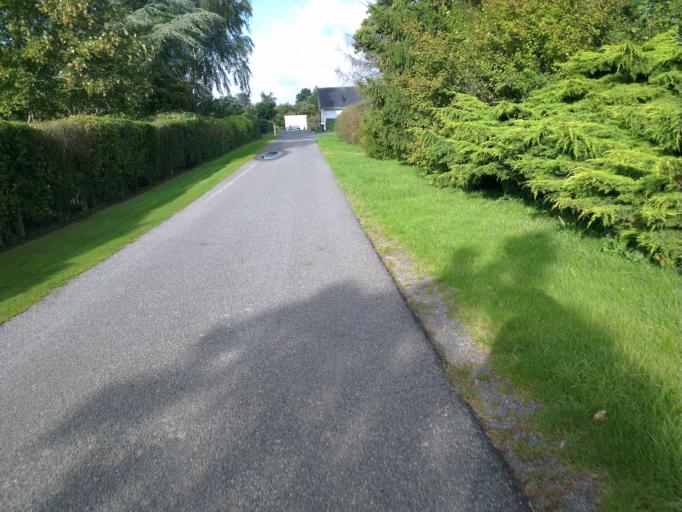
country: DK
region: Capital Region
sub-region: Frederikssund Kommune
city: Jaegerspris
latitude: 55.8297
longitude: 11.9624
